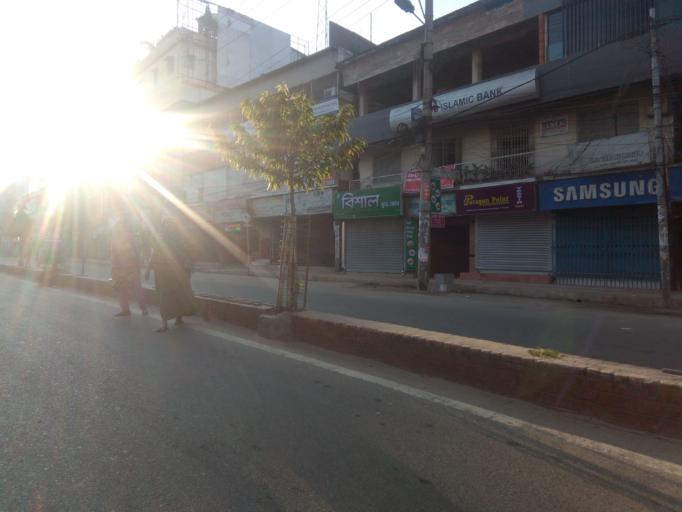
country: BD
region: Rajshahi
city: Rajshahi
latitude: 24.3653
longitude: 88.6004
